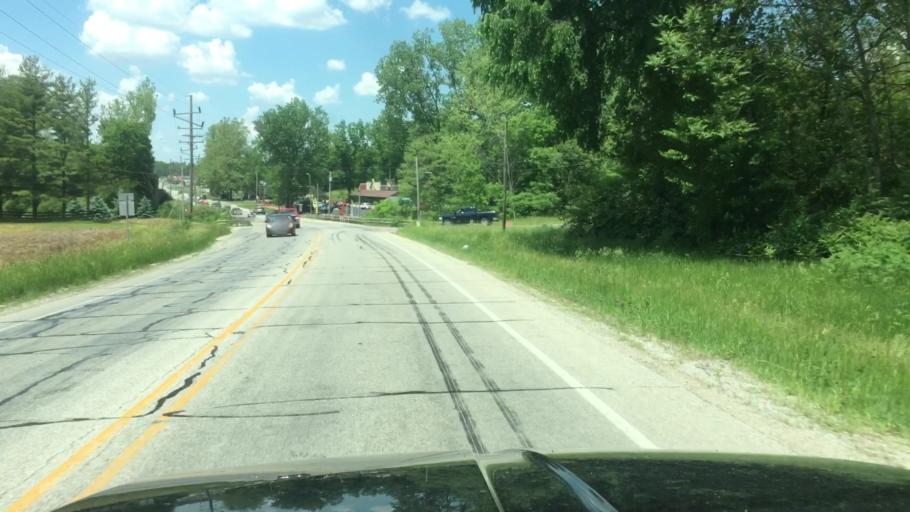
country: US
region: Indiana
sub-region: Kosciusko County
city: North Webster
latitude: 41.3154
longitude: -85.6917
